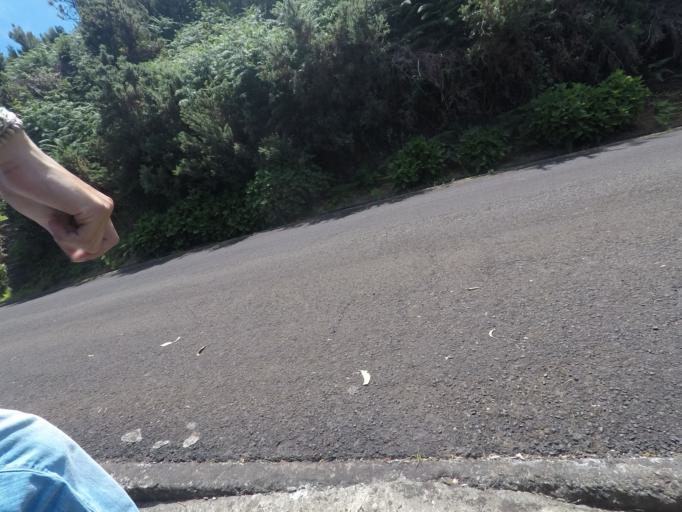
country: PT
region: Madeira
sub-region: Porto Moniz
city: Porto Moniz
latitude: 32.8447
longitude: -17.1504
